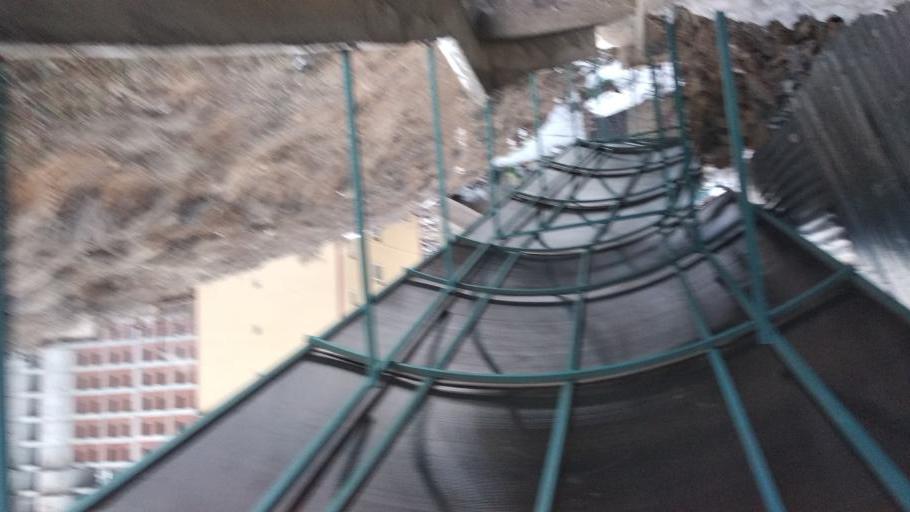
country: TR
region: Gumushane
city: Gumushkhane
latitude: 40.4374
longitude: 39.5086
